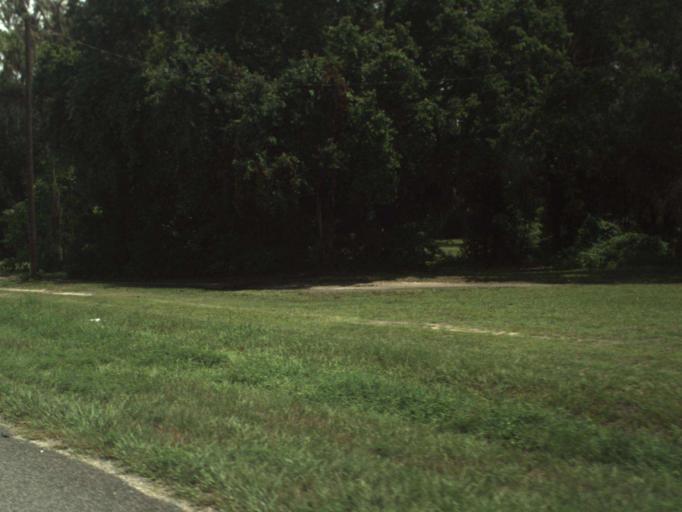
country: US
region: Florida
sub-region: Sumter County
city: Lake Panasoffkee
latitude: 28.7856
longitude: -82.0691
